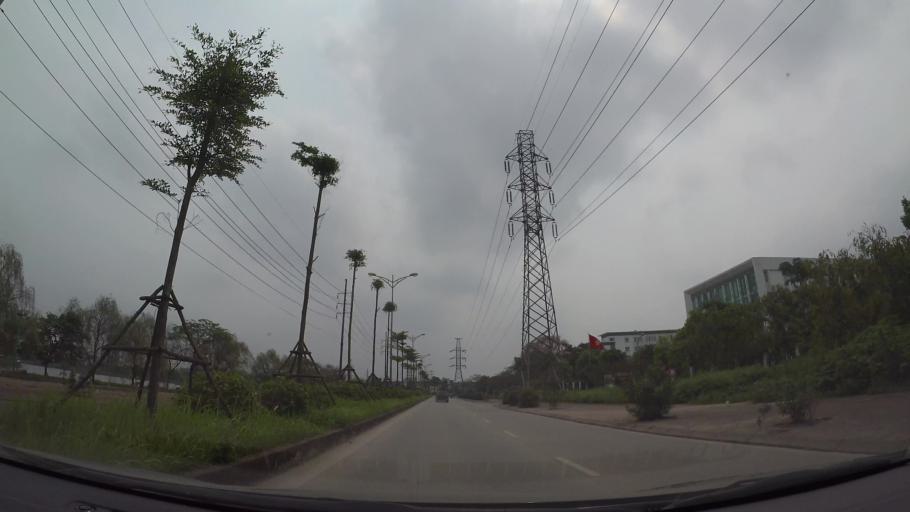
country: VN
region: Ha Noi
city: Trau Quy
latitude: 21.0634
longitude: 105.9035
